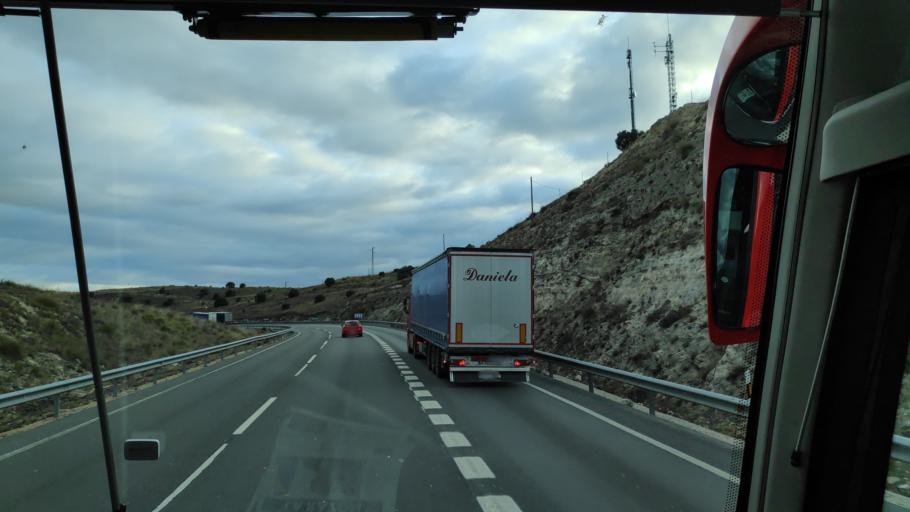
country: ES
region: Madrid
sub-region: Provincia de Madrid
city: Tielmes
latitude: 40.2019
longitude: -3.3150
